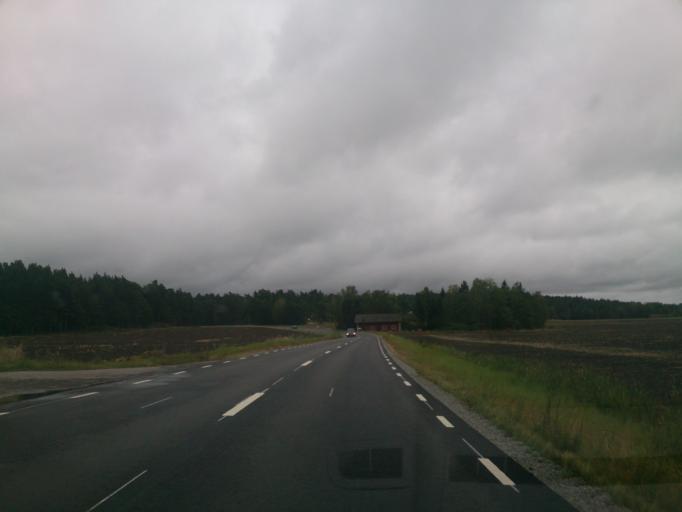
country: SE
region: OEstergoetland
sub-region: Norrkopings Kommun
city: Krokek
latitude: 58.5759
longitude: 16.5008
